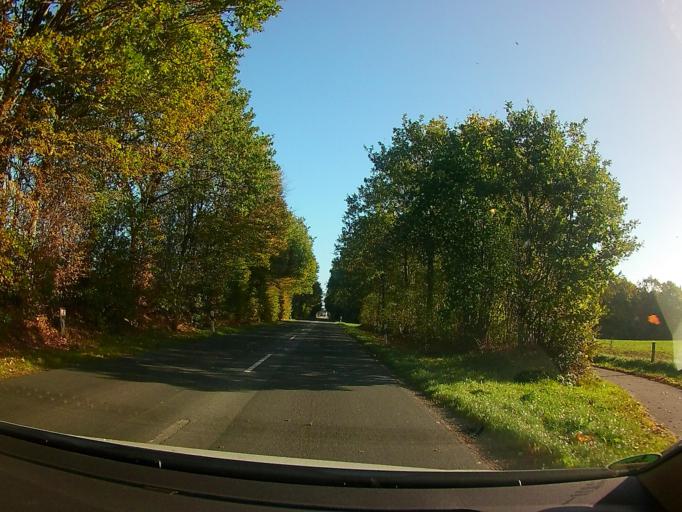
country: DE
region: Schleswig-Holstein
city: Jubek
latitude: 54.5551
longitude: 9.3782
